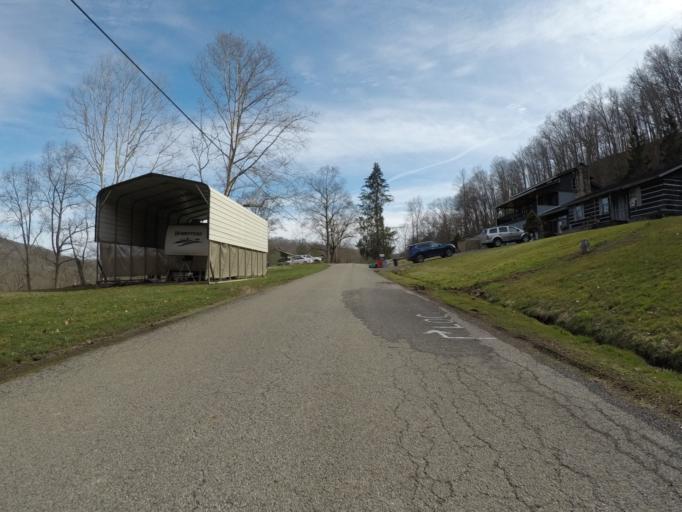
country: US
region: West Virginia
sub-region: Wayne County
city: Lavalette
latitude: 38.3409
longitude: -82.5056
